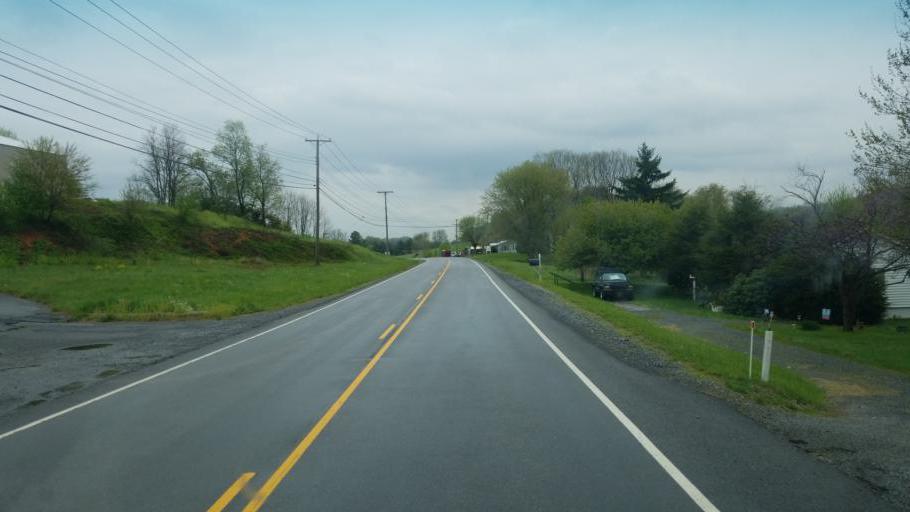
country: US
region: Virginia
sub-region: Smyth County
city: Atkins
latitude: 36.8898
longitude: -81.3527
